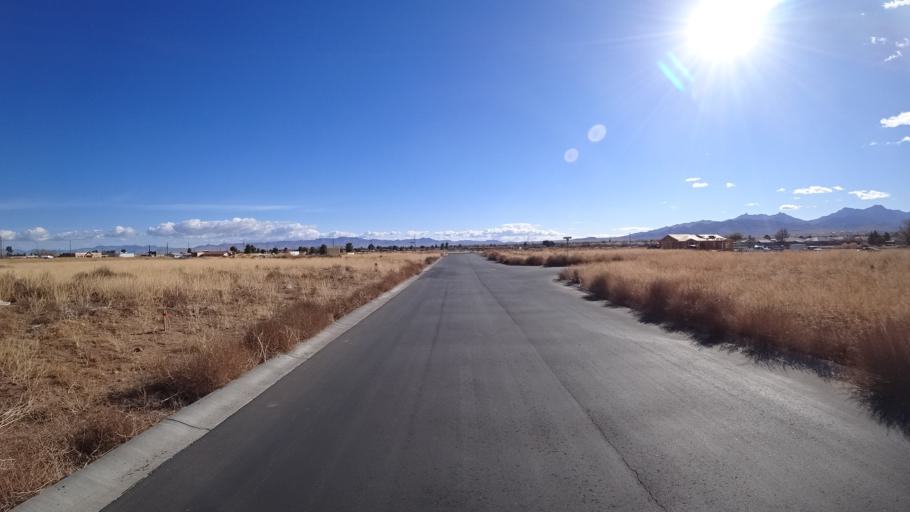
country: US
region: Arizona
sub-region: Mohave County
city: New Kingman-Butler
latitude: 35.2371
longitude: -114.0263
